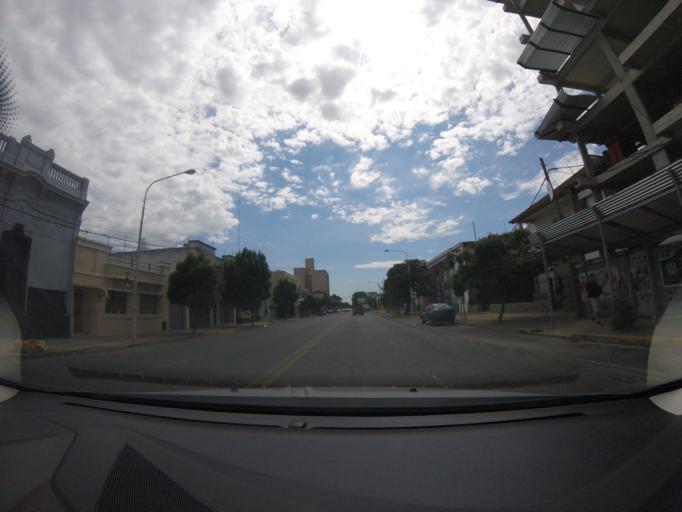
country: AR
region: Buenos Aires
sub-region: Partido de Tandil
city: Tandil
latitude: -37.3215
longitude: -59.1356
